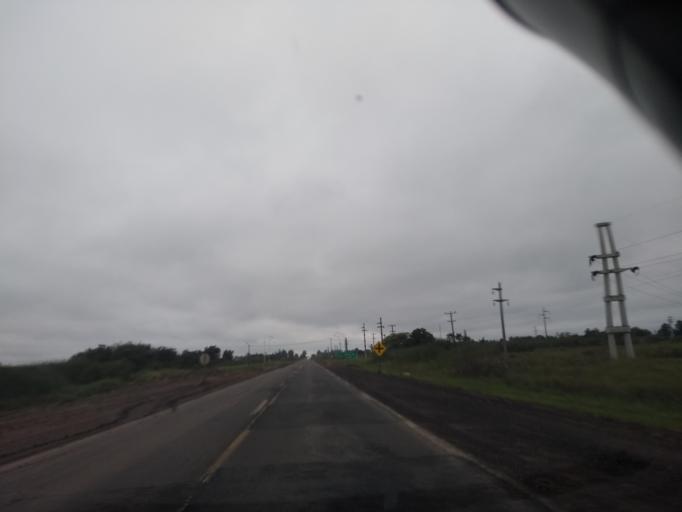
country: AR
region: Chaco
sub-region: Departamento de Quitilipi
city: Quitilipi
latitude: -26.8745
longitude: -60.2431
